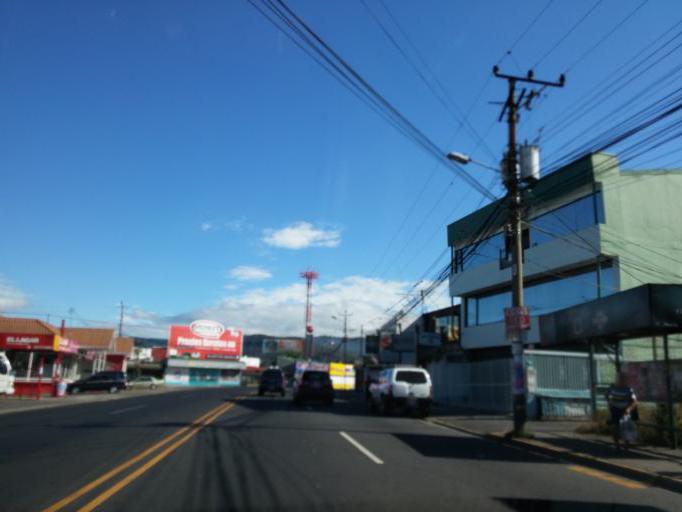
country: CR
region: San Jose
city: San Rafael Arriba
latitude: 9.9026
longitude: -84.0689
